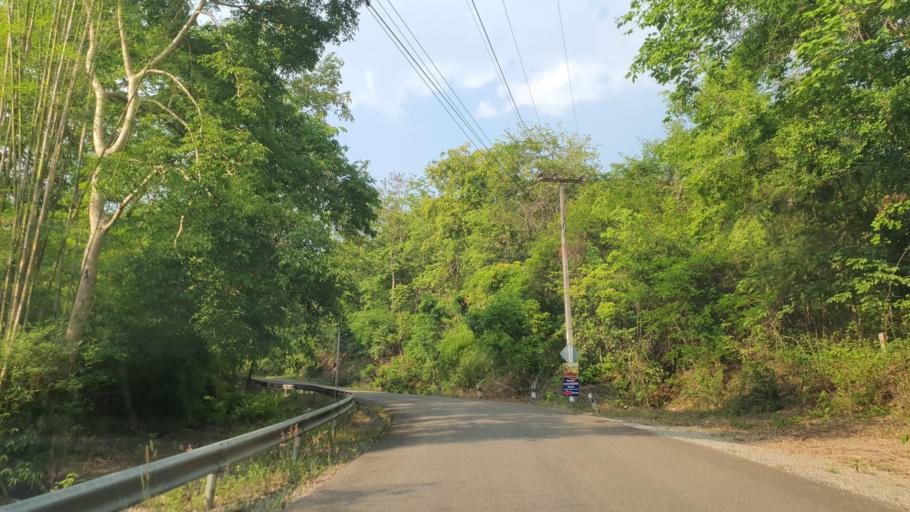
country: TH
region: Chiang Mai
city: Mae Wang
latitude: 18.6879
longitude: 98.8148
